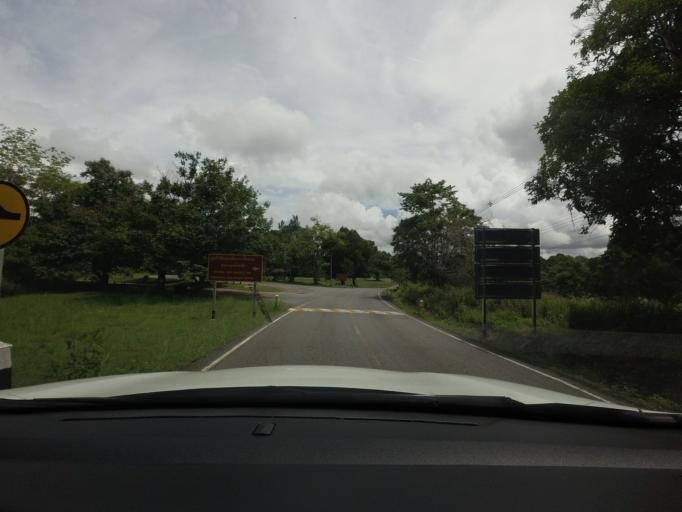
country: TH
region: Nakhon Nayok
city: Nakhon Nayok
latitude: 14.4115
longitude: 101.3725
